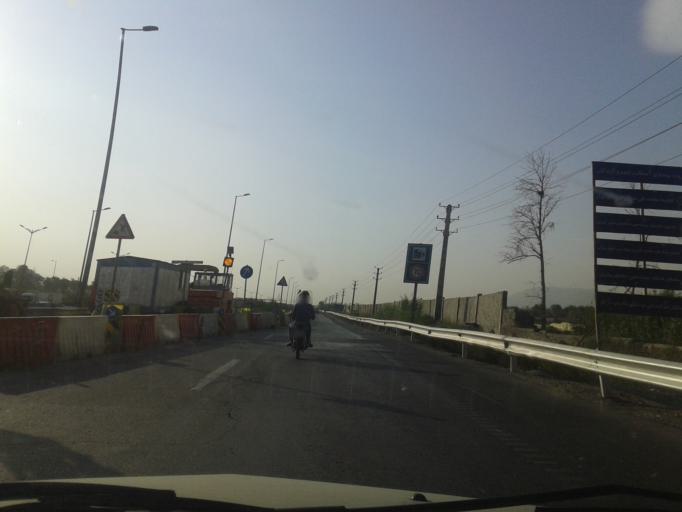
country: IR
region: Tehran
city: Eslamshahr
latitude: 35.6566
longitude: 51.2580
